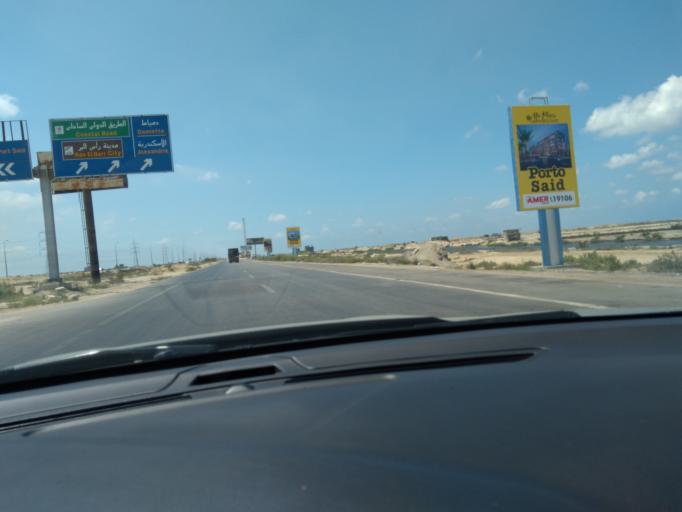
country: EG
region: Muhafazat ad Daqahliyah
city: Al Matariyah
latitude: 31.3564
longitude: 32.0461
